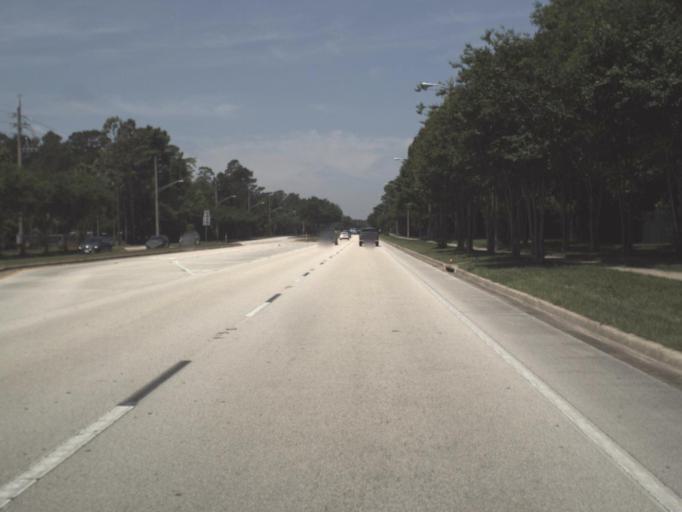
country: US
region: Florida
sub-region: Saint Johns County
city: Ponte Vedra Beach
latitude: 30.2159
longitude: -81.5226
